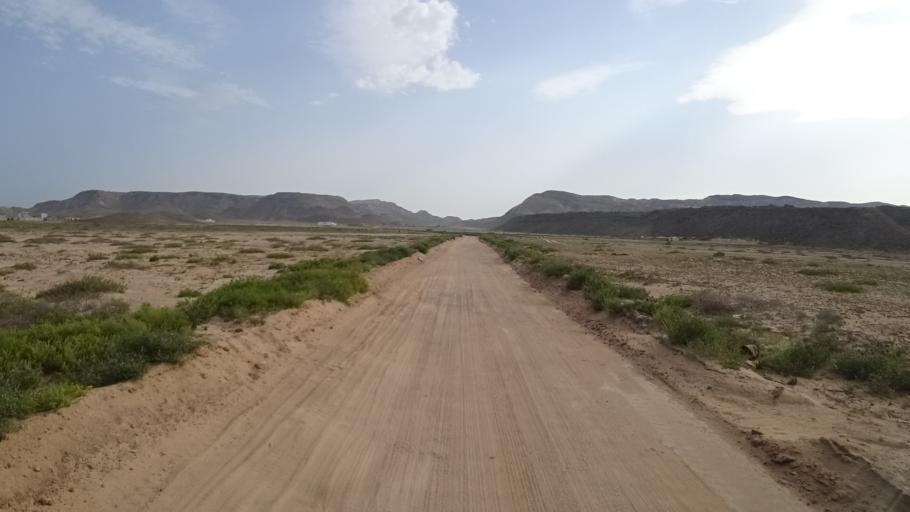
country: OM
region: Ash Sharqiyah
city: Sur
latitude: 22.4456
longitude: 59.8245
